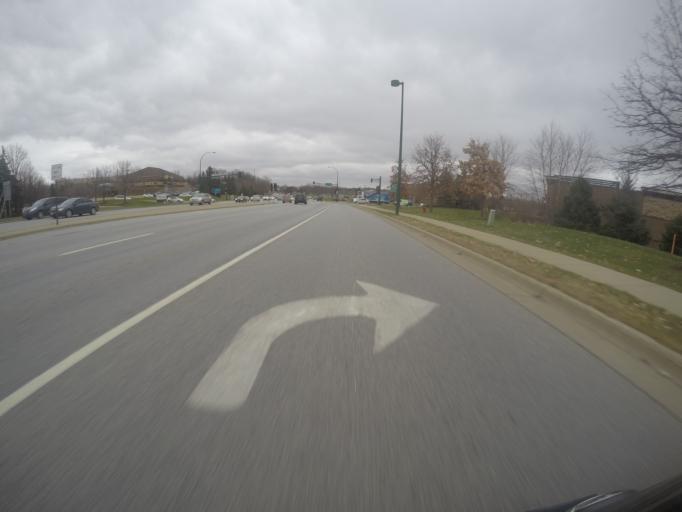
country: US
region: Minnesota
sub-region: Hennepin County
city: Eden Prairie
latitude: 44.8603
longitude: -93.4409
